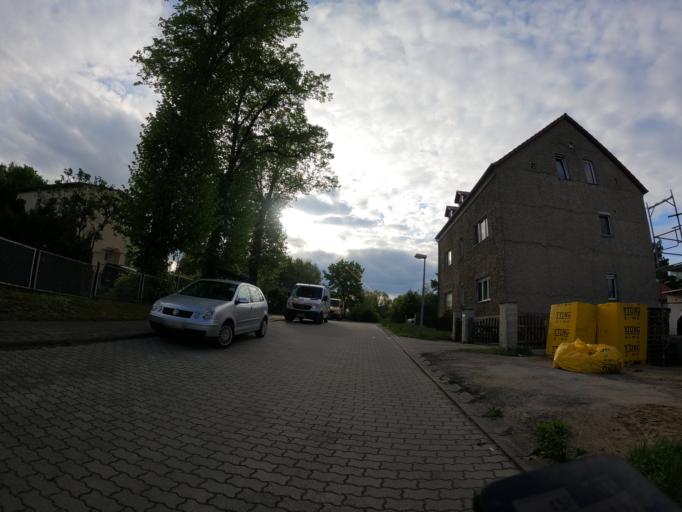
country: DE
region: Brandenburg
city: Konigs Wusterhausen
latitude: 52.3054
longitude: 13.6510
